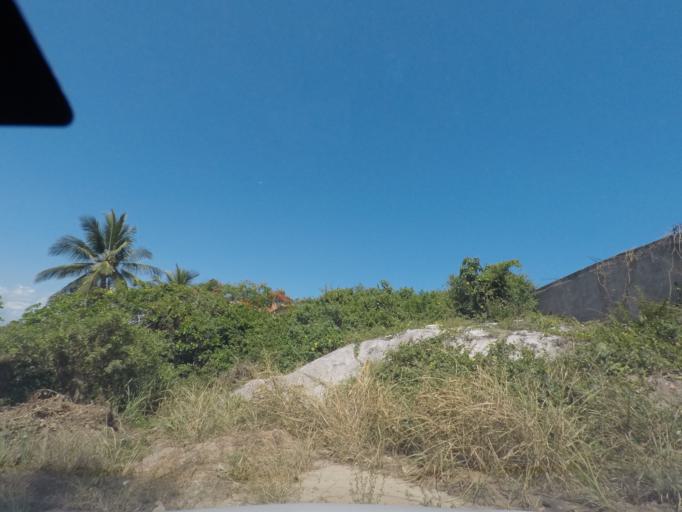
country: BR
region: Rio de Janeiro
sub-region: Marica
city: Marica
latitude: -22.9733
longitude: -42.9261
